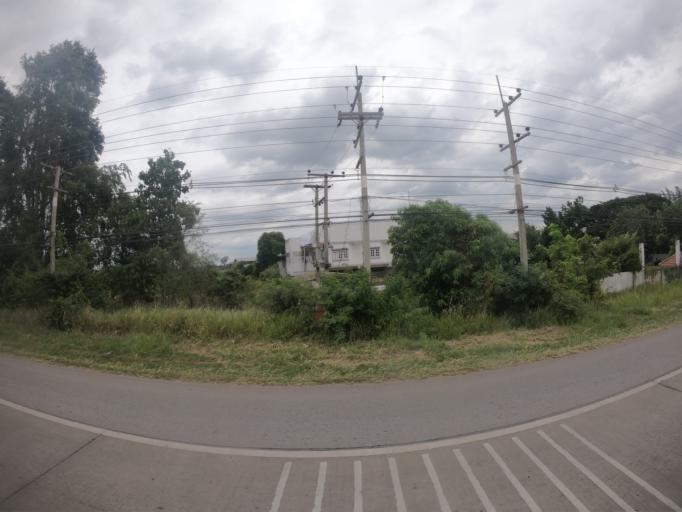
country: TH
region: Nakhon Ratchasima
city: Chok Chai
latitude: 14.7914
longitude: 102.1678
